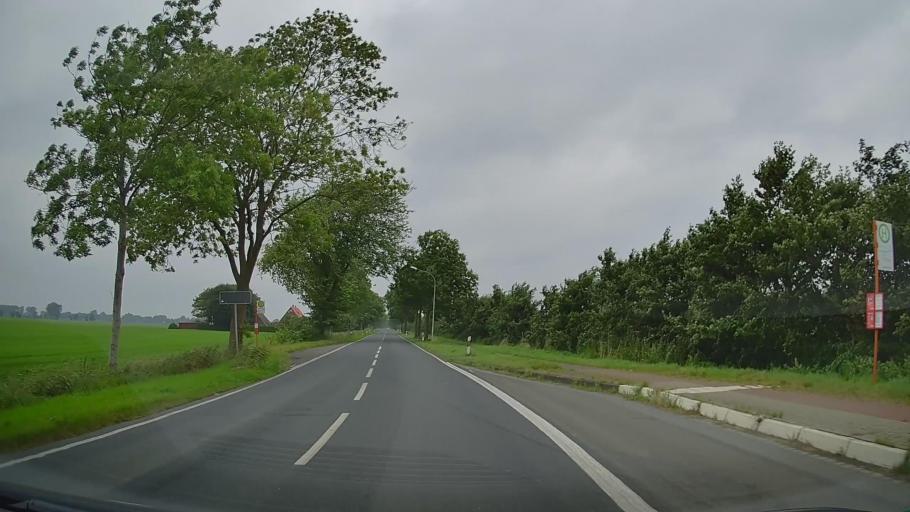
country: DE
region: Lower Saxony
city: Balje
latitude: 53.8123
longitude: 9.1304
